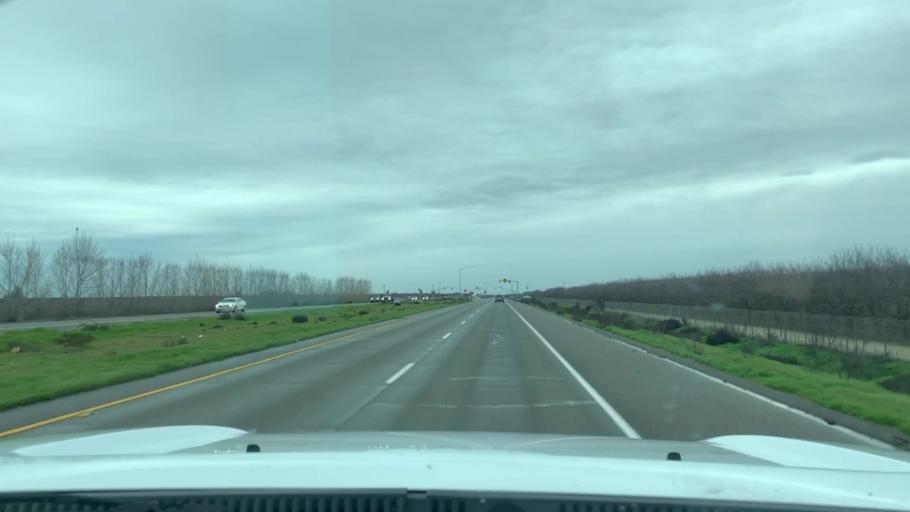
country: US
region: California
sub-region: Fresno County
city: Caruthers
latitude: 36.5138
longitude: -119.7860
